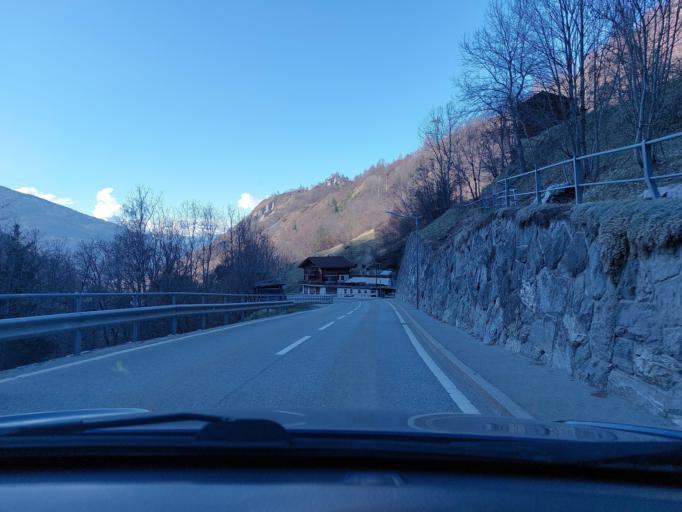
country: CH
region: Valais
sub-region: Herens District
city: Evolene
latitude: 46.1517
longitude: 7.4537
